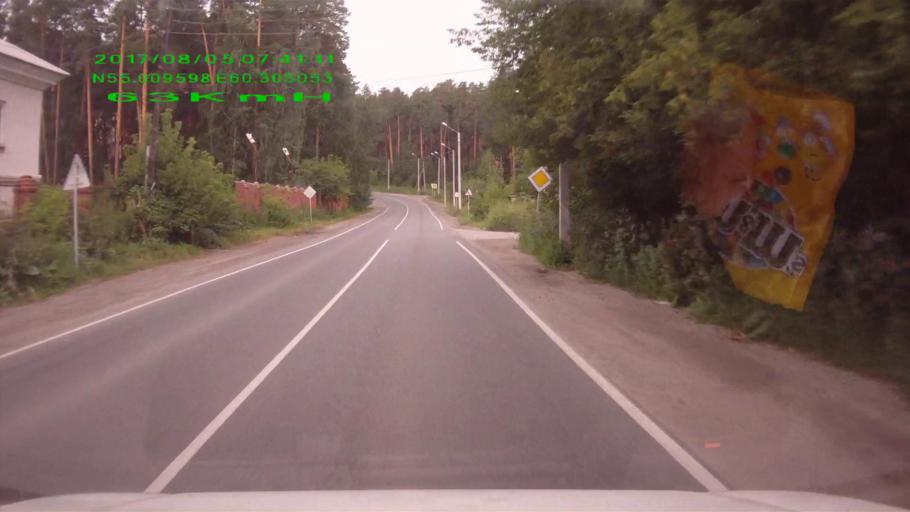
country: RU
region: Chelyabinsk
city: Chebarkul'
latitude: 55.0097
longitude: 60.3046
